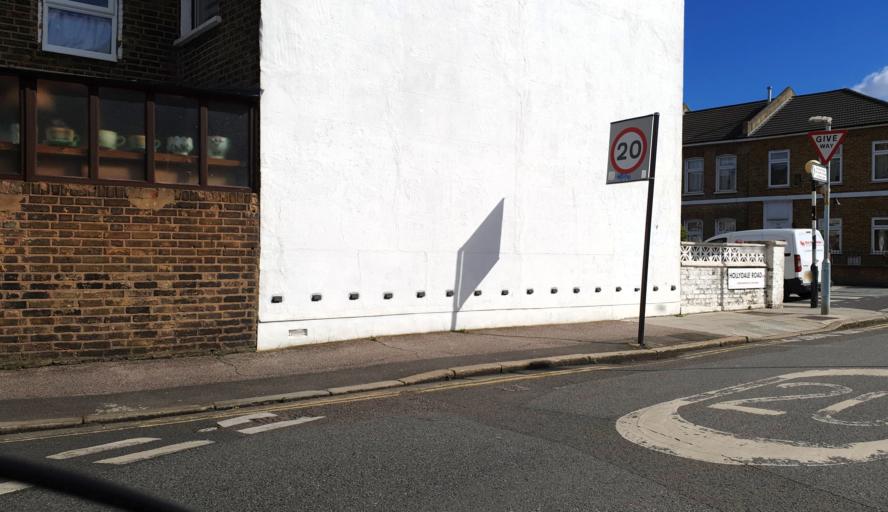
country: GB
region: England
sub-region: Greater London
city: Camberwell
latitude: 51.4679
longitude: -0.0543
